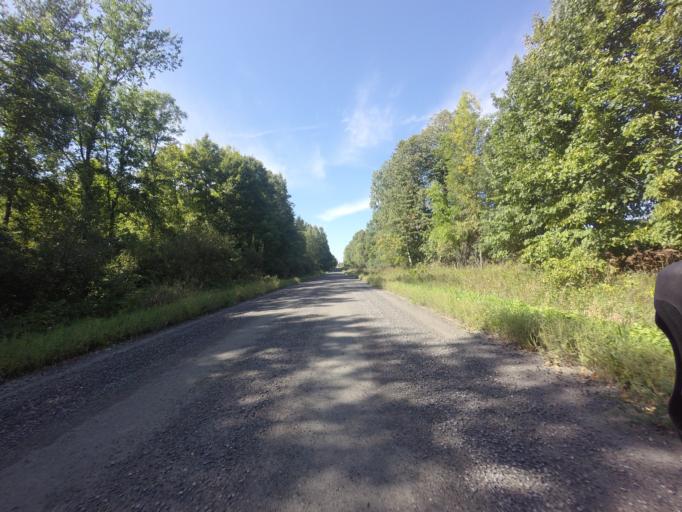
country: CA
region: Ontario
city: Perth
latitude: 44.9592
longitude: -76.3365
